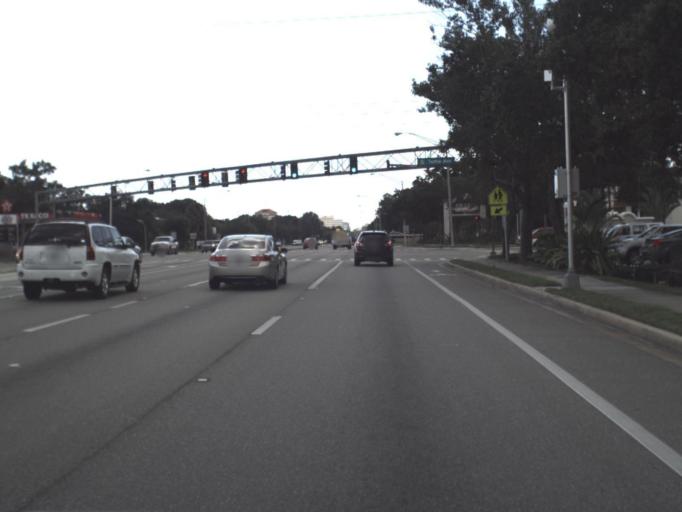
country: US
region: Florida
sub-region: Sarasota County
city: Sarasota
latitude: 27.3377
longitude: -82.5132
